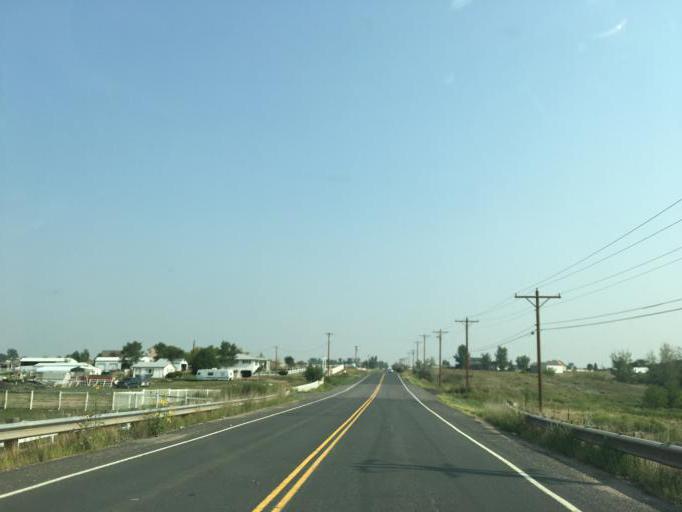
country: US
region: Colorado
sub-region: Adams County
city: Todd Creek
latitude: 39.9786
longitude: -104.8655
